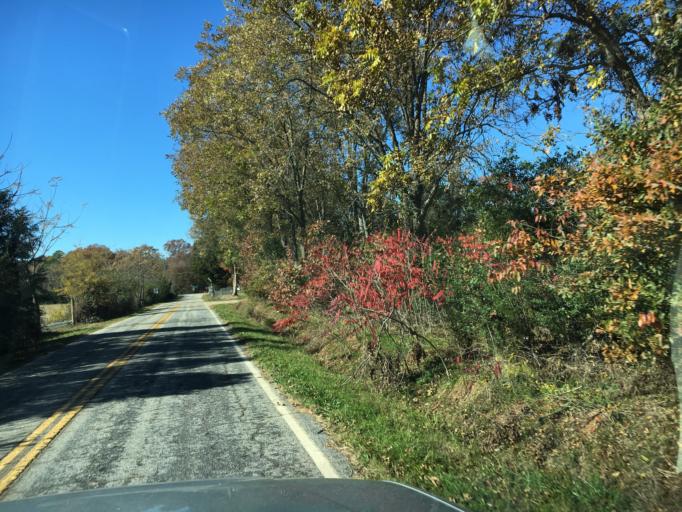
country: US
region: Georgia
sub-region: Hart County
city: Reed Creek
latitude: 34.3910
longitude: -82.8060
